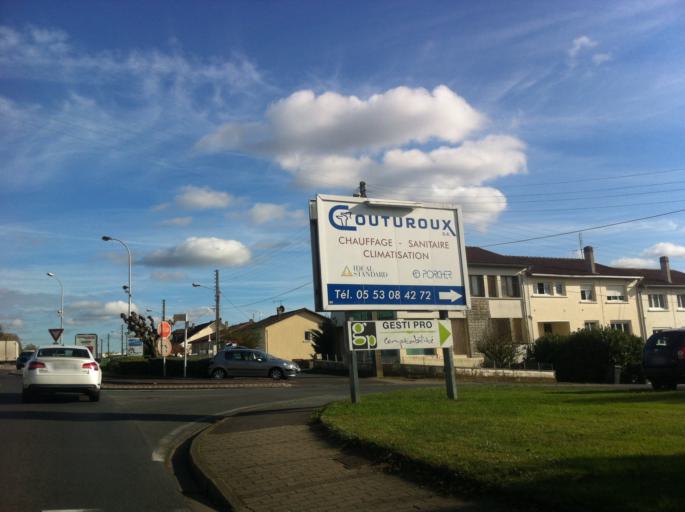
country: FR
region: Aquitaine
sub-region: Departement de la Dordogne
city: Perigueux
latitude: 45.1906
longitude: 0.7396
